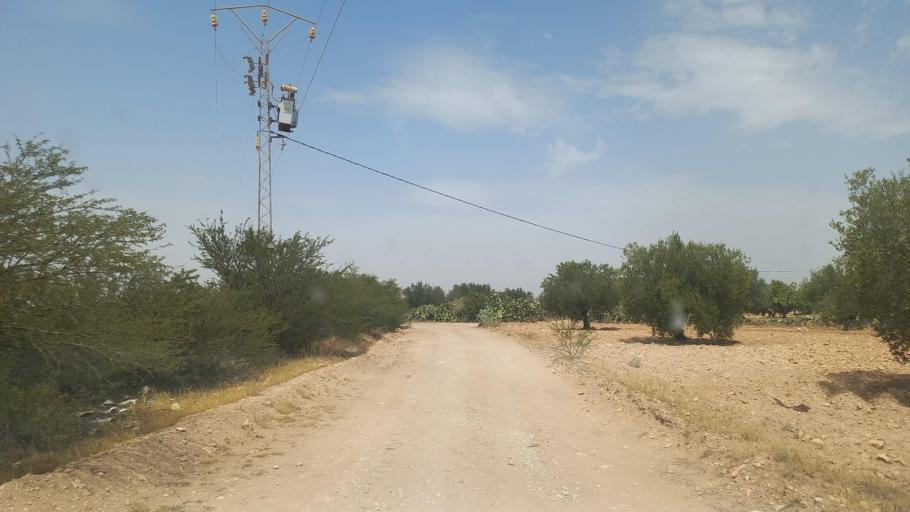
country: TN
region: Al Qasrayn
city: Kasserine
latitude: 35.2558
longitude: 9.0063
